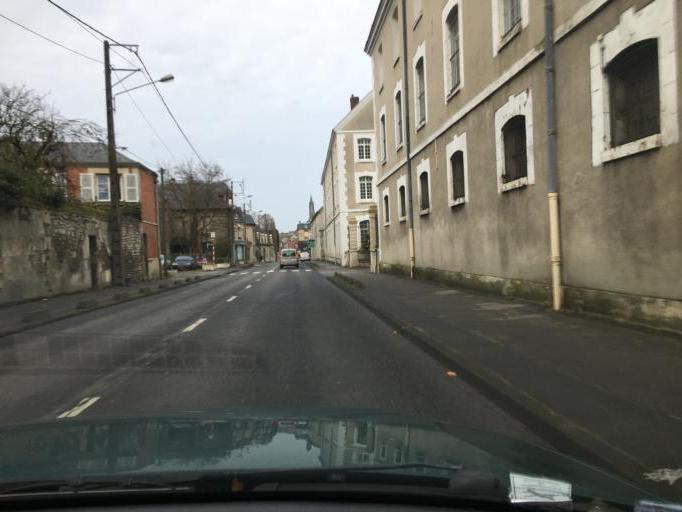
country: FR
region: Picardie
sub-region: Departement de l'Oise
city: Senlis
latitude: 49.1995
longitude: 2.5797
